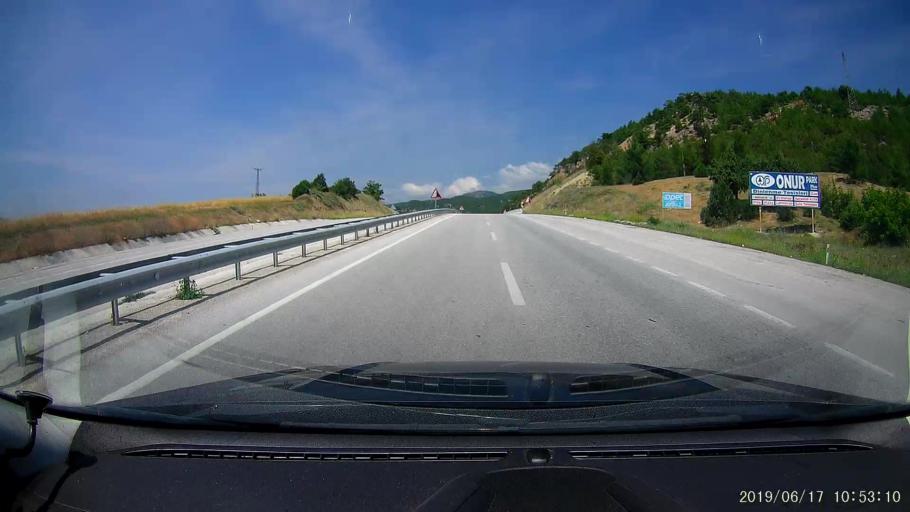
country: TR
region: Corum
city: Hacihamza
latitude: 41.0831
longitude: 34.3279
